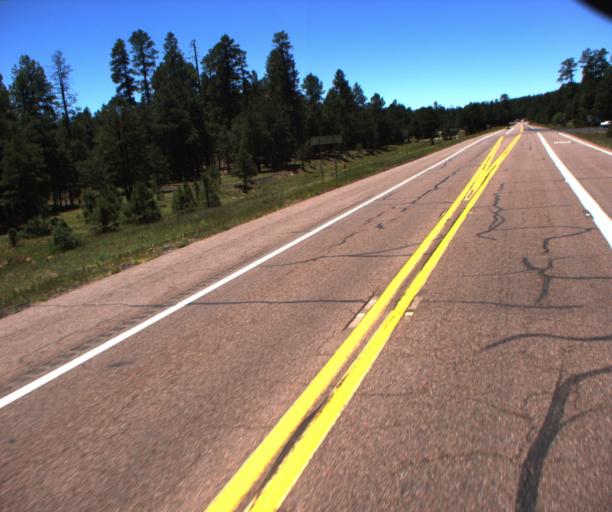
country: US
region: Arizona
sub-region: Gila County
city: Pine
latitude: 34.5502
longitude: -111.3137
